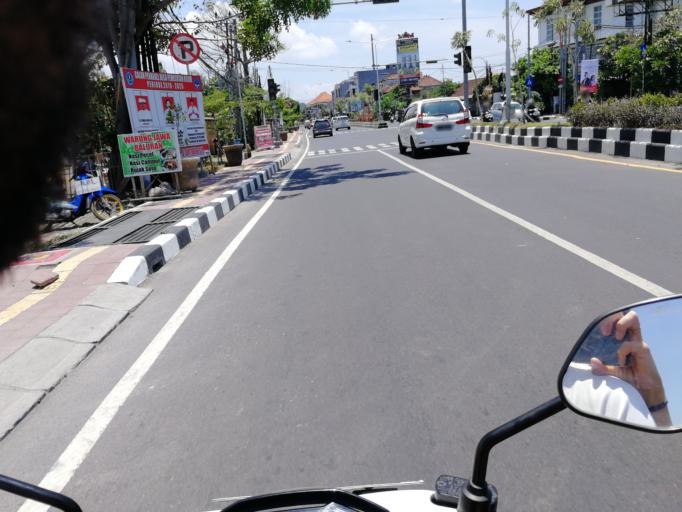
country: ID
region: Bali
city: Kuta
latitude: -8.6958
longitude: 115.1868
